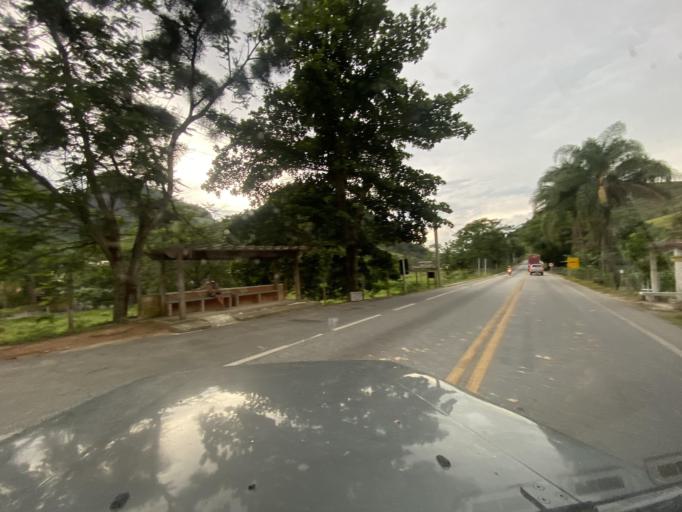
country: BR
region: Espirito Santo
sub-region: Jeronimo Monteiro
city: Jeronimo Monteiro
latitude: -20.7982
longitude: -41.3491
